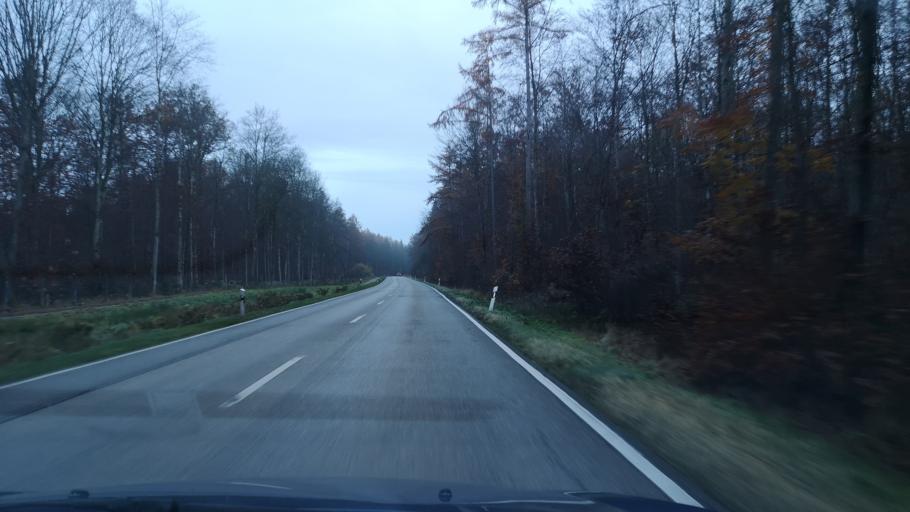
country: DE
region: Bavaria
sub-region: Upper Bavaria
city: Ebersberg
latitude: 48.1196
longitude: 11.9498
